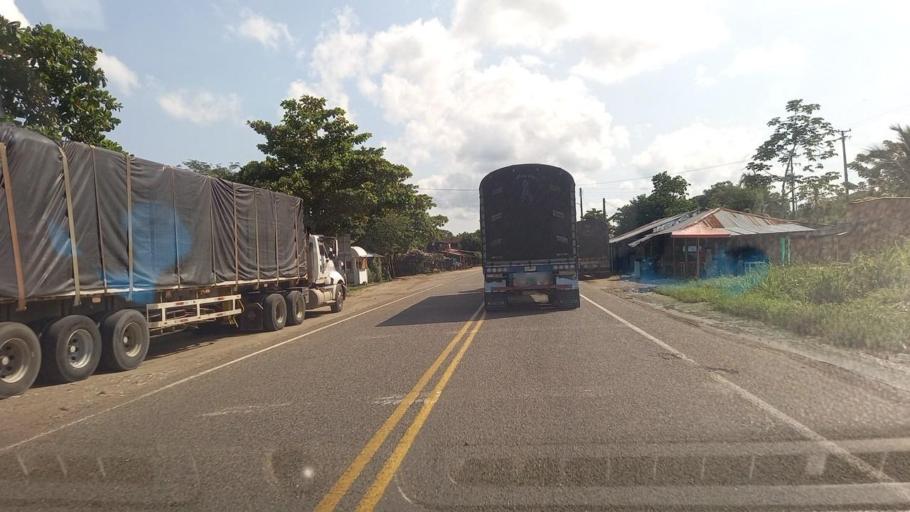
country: CO
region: Antioquia
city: Puerto Berrio
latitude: 6.3309
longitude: -74.4353
